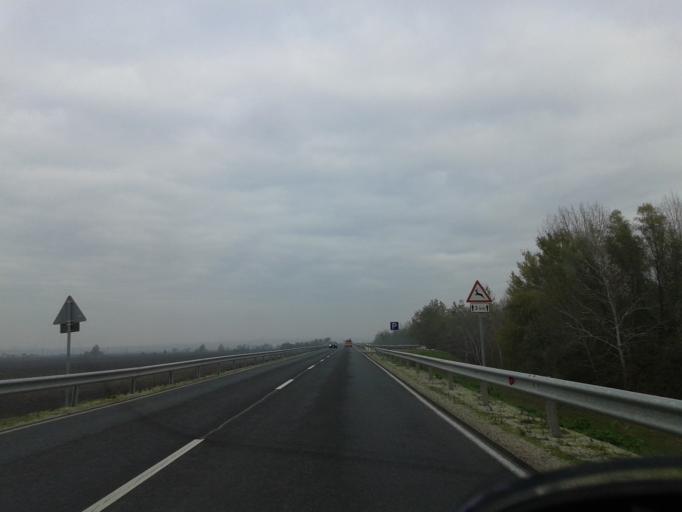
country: HU
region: Fejer
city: Ercsi
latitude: 47.2134
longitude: 18.8851
